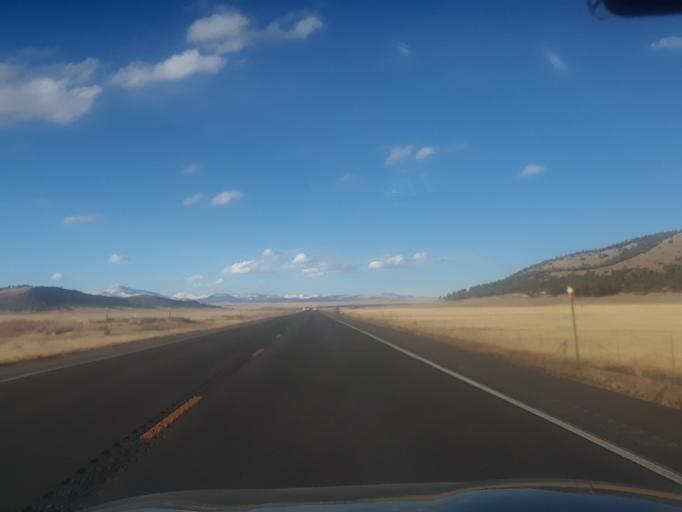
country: US
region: Colorado
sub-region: Chaffee County
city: Buena Vista
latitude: 38.9476
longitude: -105.9633
